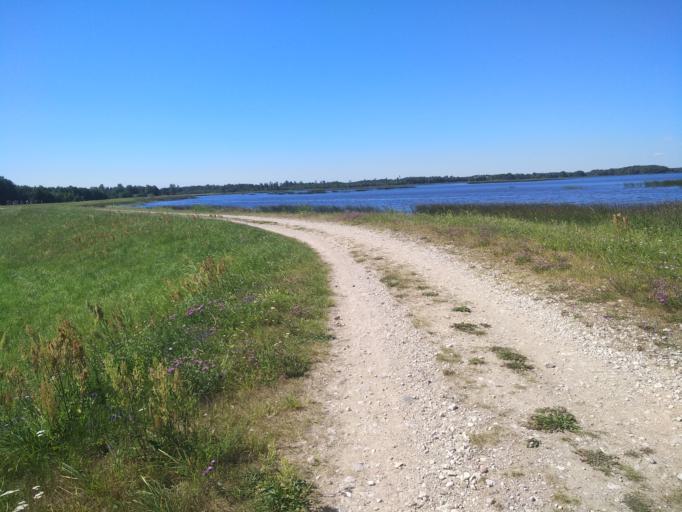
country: EE
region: Harju
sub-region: Anija vald
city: Kehra
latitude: 59.1072
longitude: 25.3737
